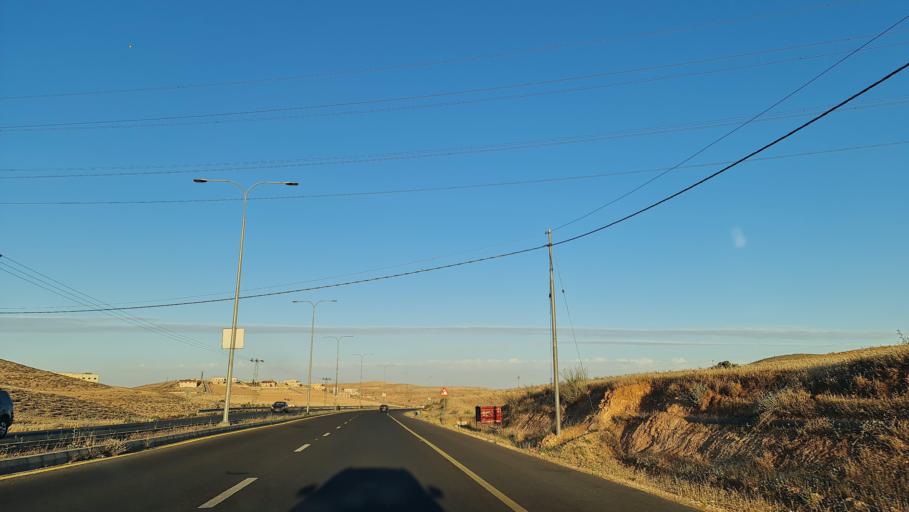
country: JO
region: Zarqa
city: Russeifa
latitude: 32.0876
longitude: 35.9972
